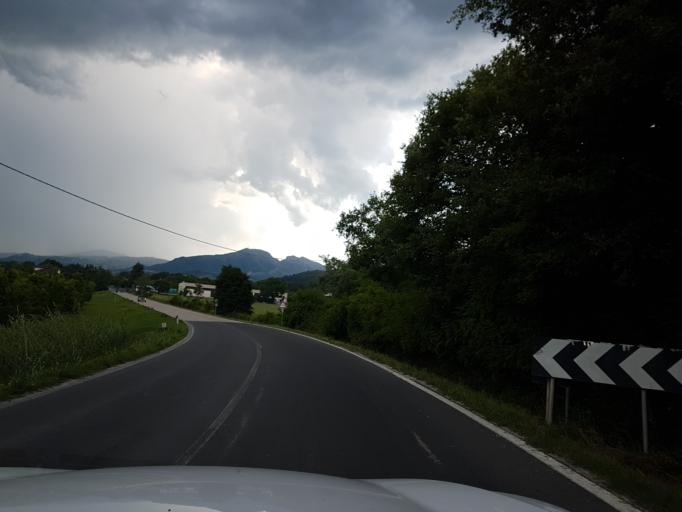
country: IT
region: Emilia-Romagna
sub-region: Provincia di Rimini
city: Secchiano
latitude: 43.9357
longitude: 12.3376
